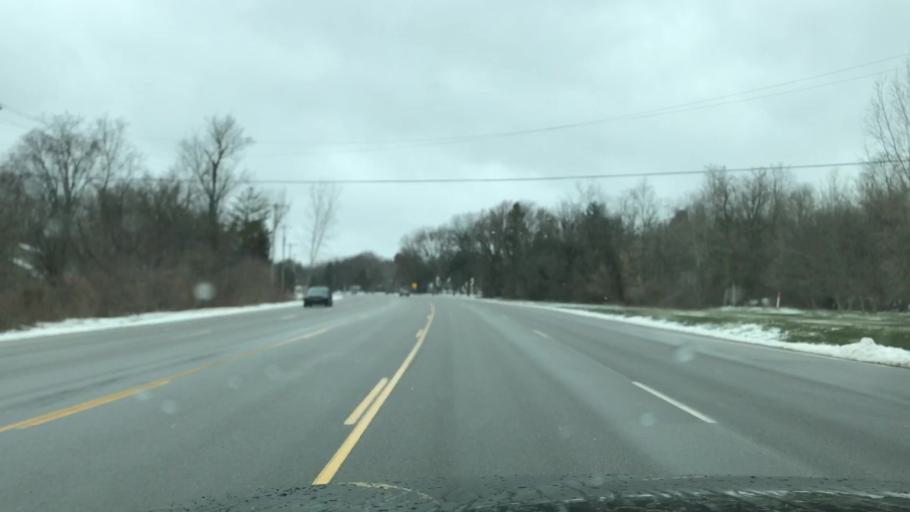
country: US
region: Michigan
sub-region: Kent County
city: Forest Hills
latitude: 42.9228
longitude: -85.5069
